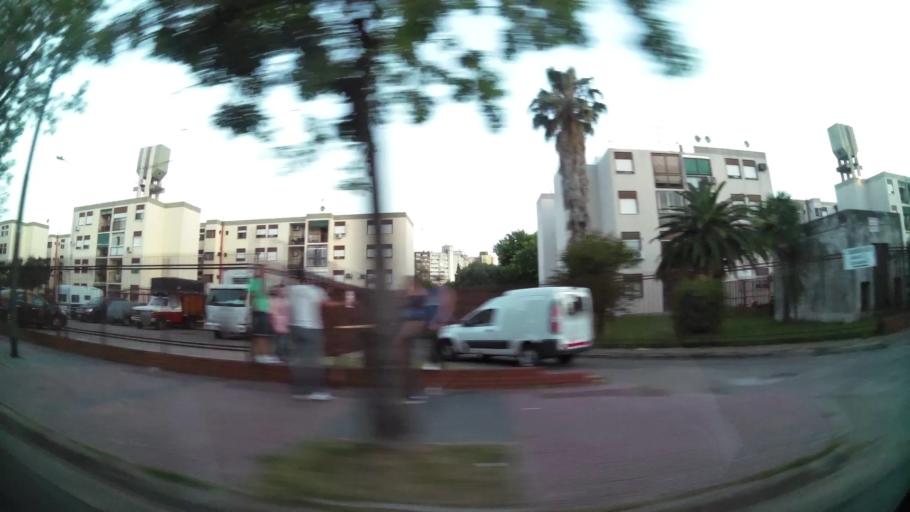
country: AR
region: Buenos Aires F.D.
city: Villa Lugano
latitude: -34.6825
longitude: -58.4709
